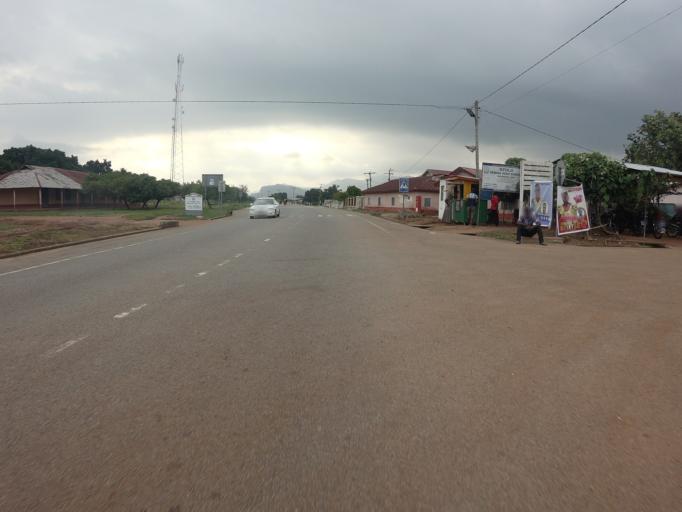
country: GH
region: Volta
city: Ho
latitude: 6.7729
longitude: 0.4793
